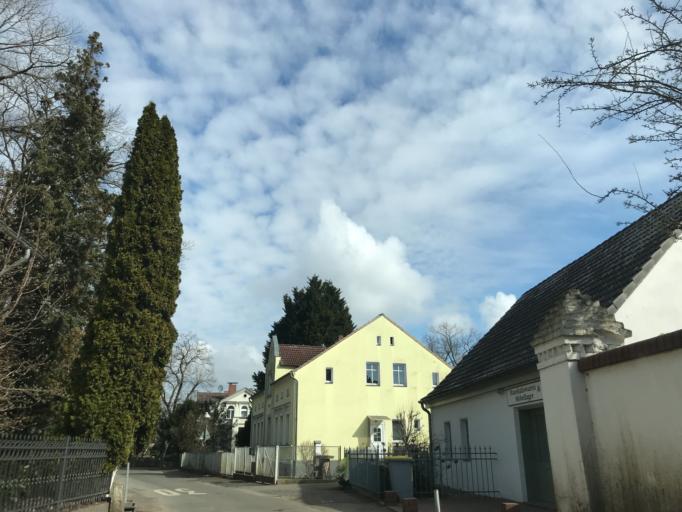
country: DE
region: Berlin
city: Kladow
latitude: 52.4506
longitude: 13.1438
